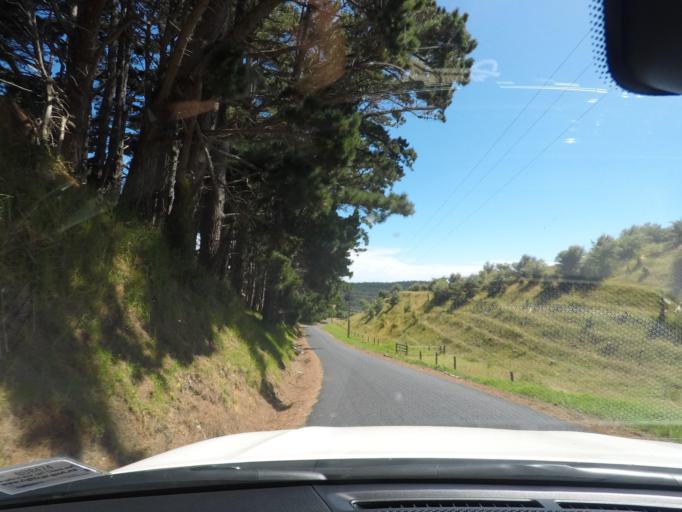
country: NZ
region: Auckland
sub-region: Auckland
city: Parakai
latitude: -36.5897
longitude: 174.2878
